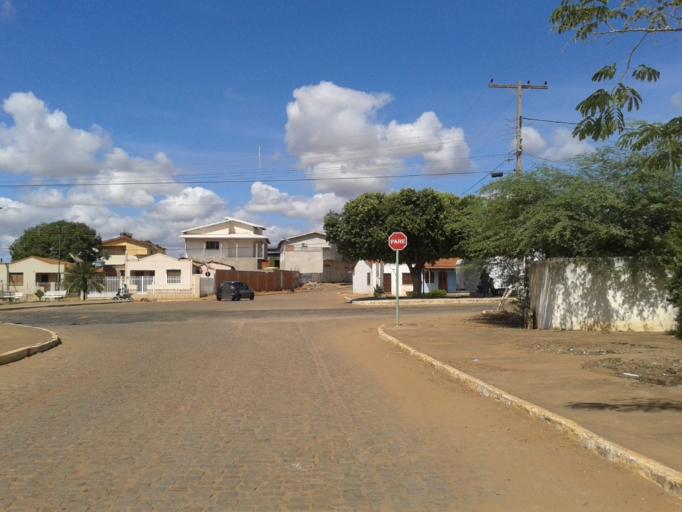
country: BR
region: Bahia
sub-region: Livramento Do Brumado
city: Livramento do Brumado
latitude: -13.6567
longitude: -41.8485
